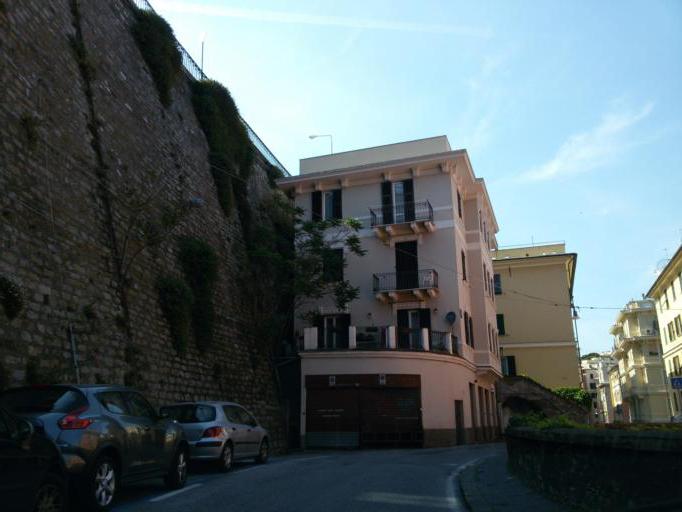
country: IT
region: Liguria
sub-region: Provincia di Genova
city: San Teodoro
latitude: 44.4014
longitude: 8.9411
